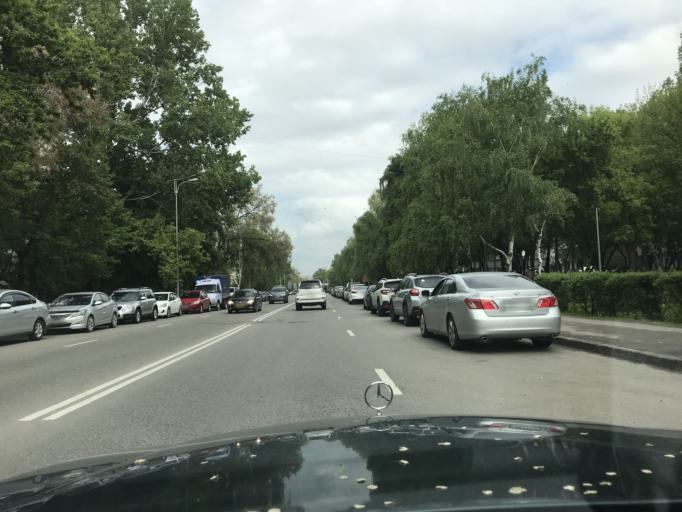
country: KZ
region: Almaty Qalasy
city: Almaty
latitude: 43.2053
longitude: 76.8729
